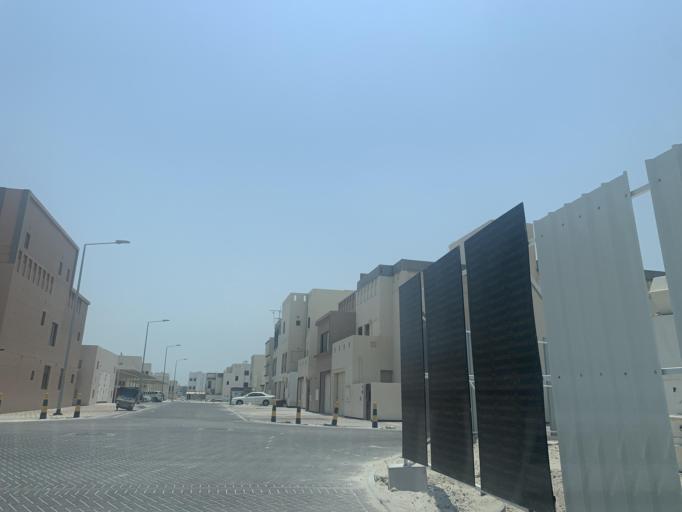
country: BH
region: Muharraq
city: Al Hadd
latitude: 26.2337
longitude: 50.6764
